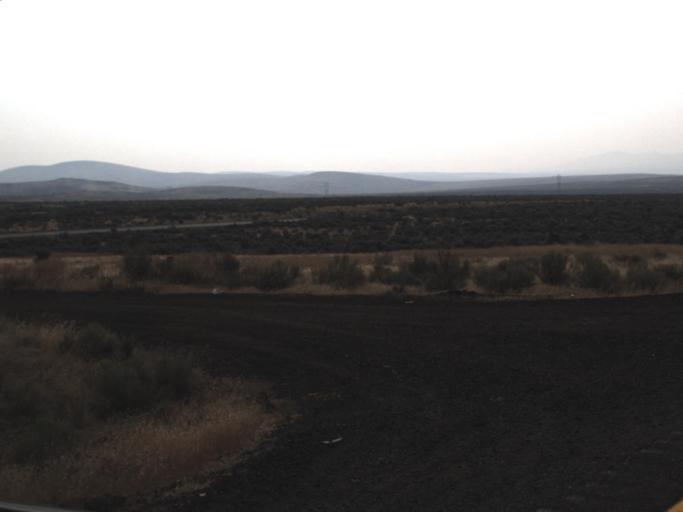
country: US
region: Washington
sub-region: Kittitas County
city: Kittitas
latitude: 46.8391
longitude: -120.3734
